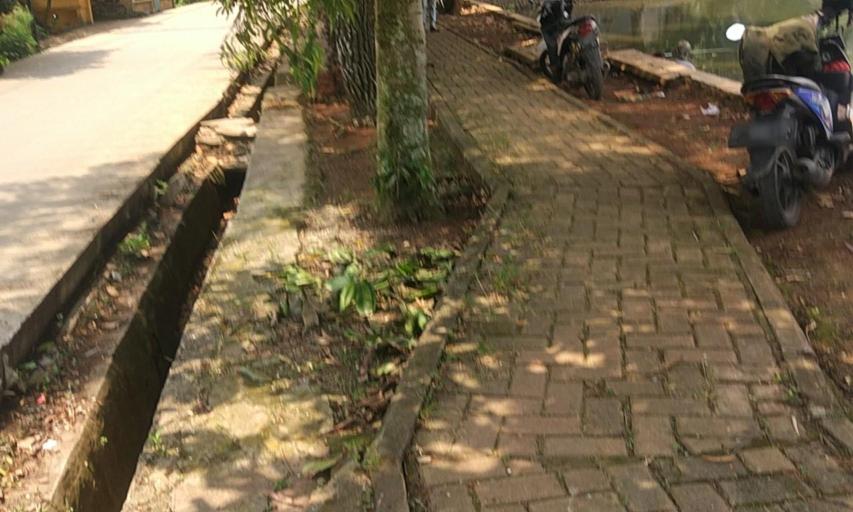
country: ID
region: West Java
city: Ciampea
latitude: -6.5292
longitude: 106.7273
